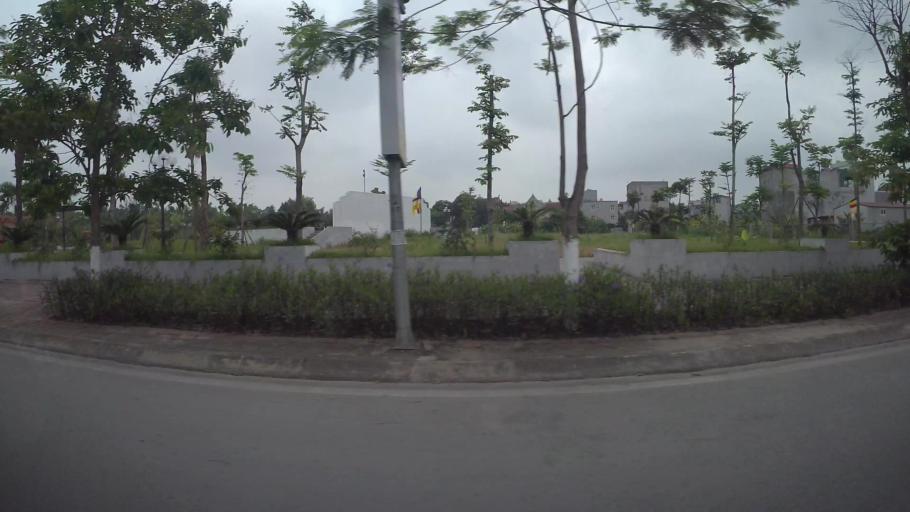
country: VN
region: Ha Noi
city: Trau Quy
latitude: 21.0541
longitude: 105.9196
